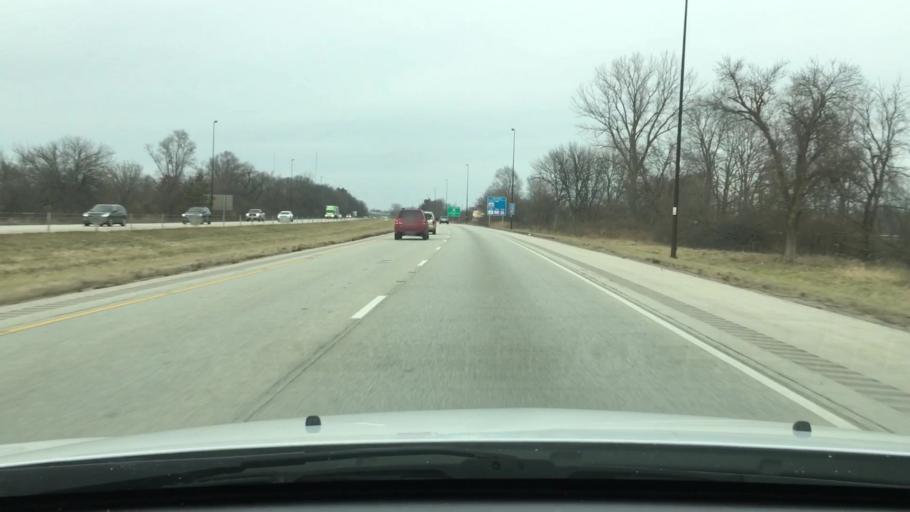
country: US
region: Illinois
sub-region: Sangamon County
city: Grandview
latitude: 39.8098
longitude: -89.5930
